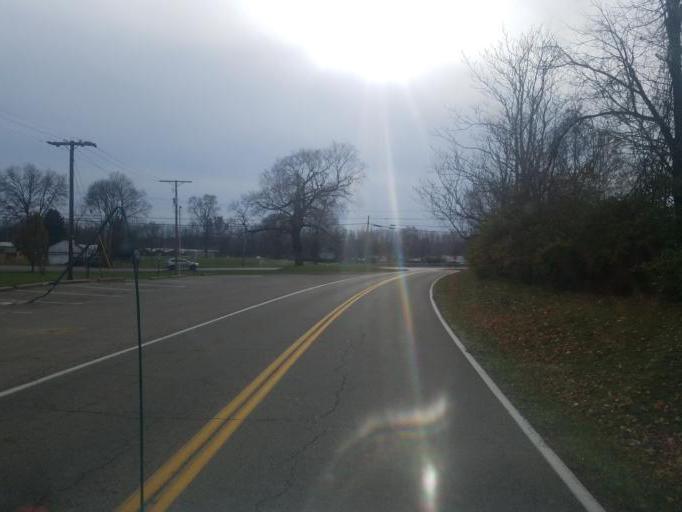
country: US
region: Ohio
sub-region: Knox County
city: Mount Vernon
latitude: 40.3952
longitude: -82.5025
